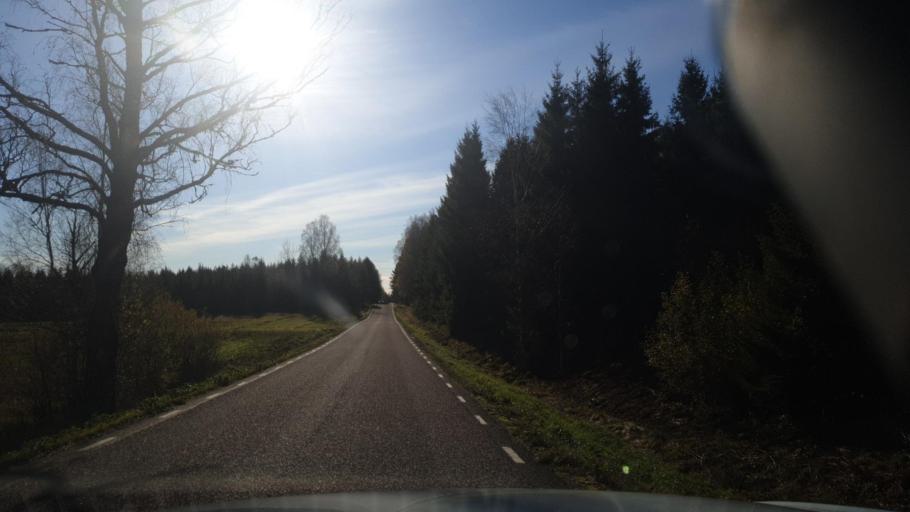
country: SE
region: Vaermland
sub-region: Karlstads Kommun
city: Edsvalla
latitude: 59.5141
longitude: 13.1104
